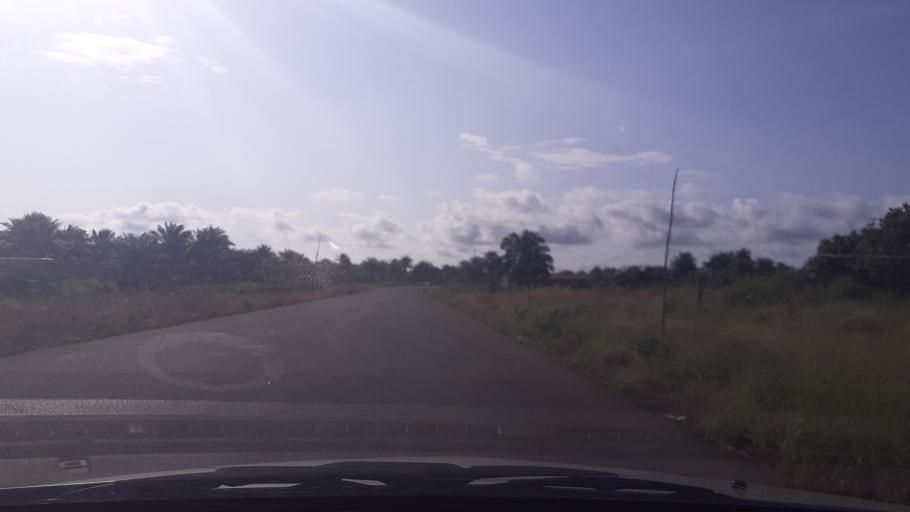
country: LR
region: Montserrado
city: Bensonville City
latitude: 6.1691
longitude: -10.4480
